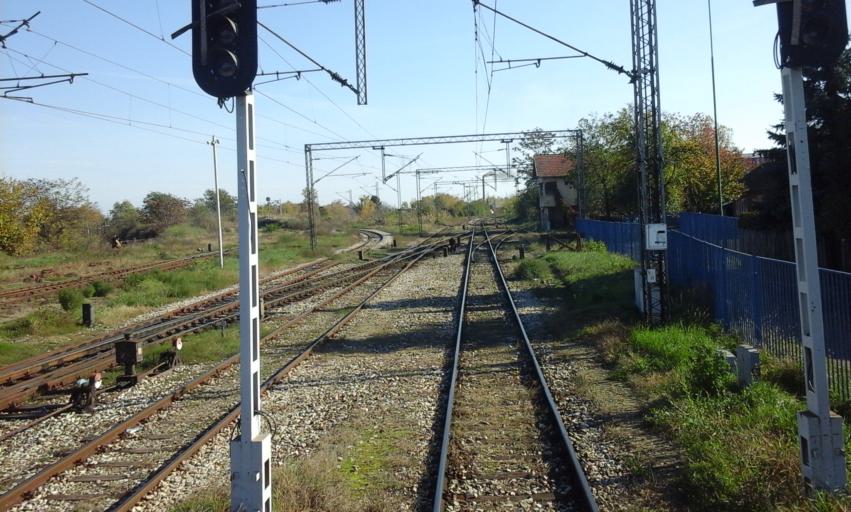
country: RS
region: Autonomna Pokrajina Vojvodina
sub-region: Severnobacki Okrug
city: Subotica
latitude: 46.0934
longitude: 19.6795
